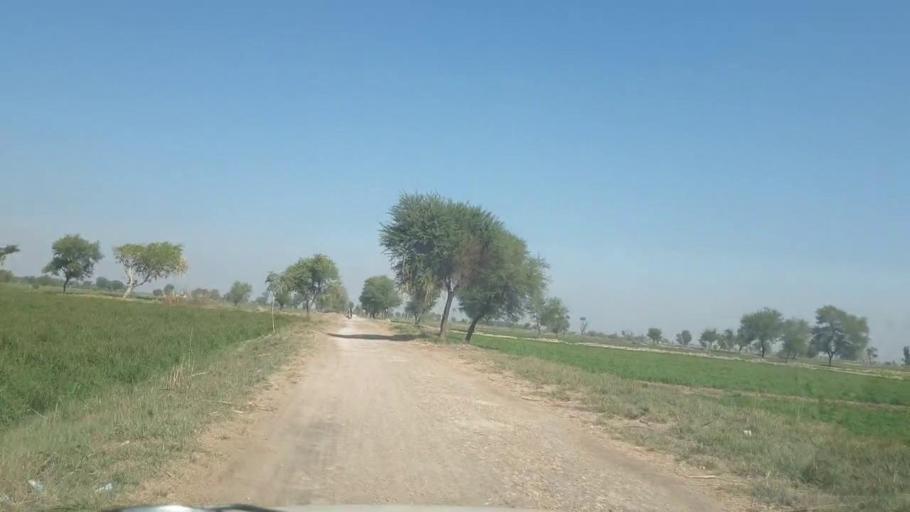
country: PK
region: Sindh
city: Mirpur Khas
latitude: 25.5502
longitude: 69.1965
